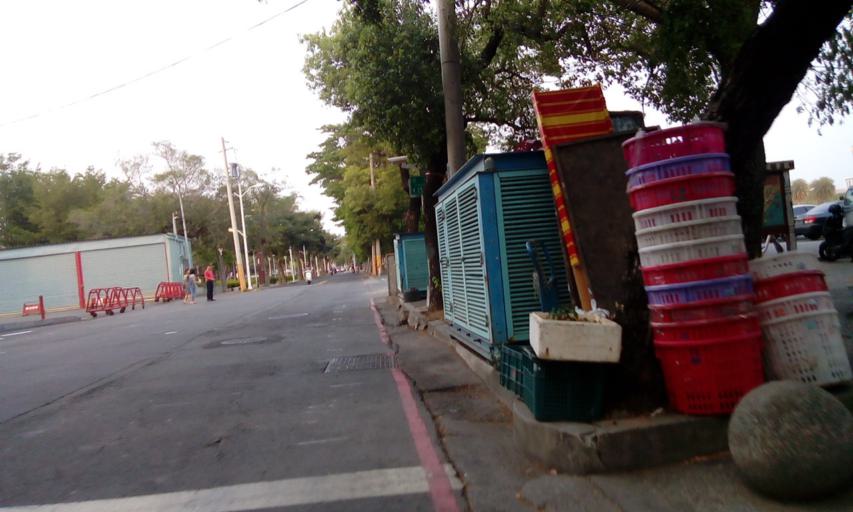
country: TW
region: Kaohsiung
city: Kaohsiung
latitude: 22.6863
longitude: 120.2962
